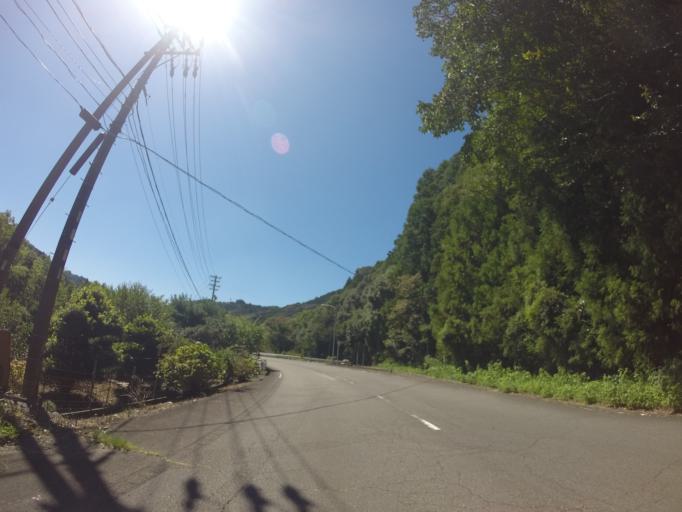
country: JP
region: Shizuoka
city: Fujieda
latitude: 34.9490
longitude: 138.2101
